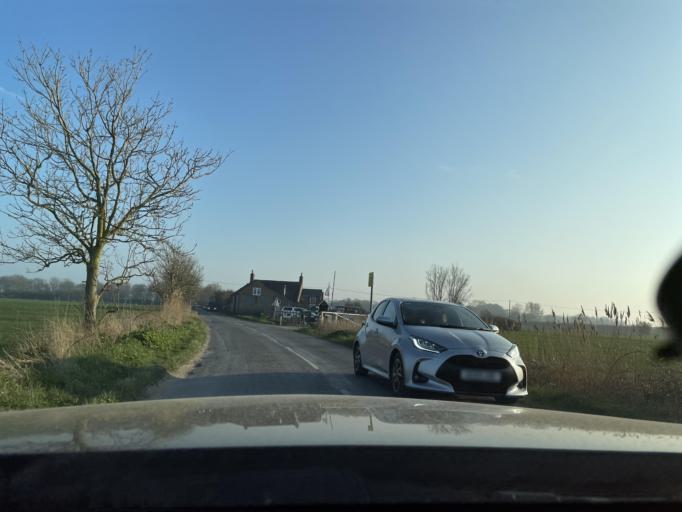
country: GB
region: England
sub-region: Norfolk
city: Martham
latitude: 52.7541
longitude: 1.6447
